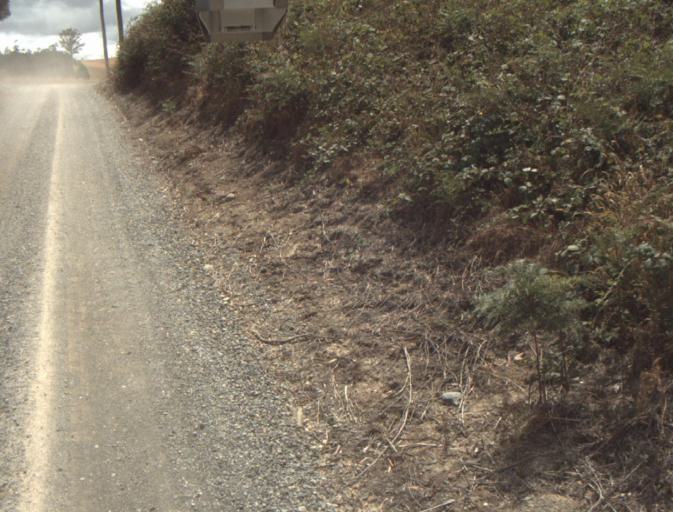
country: AU
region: Tasmania
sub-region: Launceston
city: Mayfield
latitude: -41.1940
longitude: 147.1704
